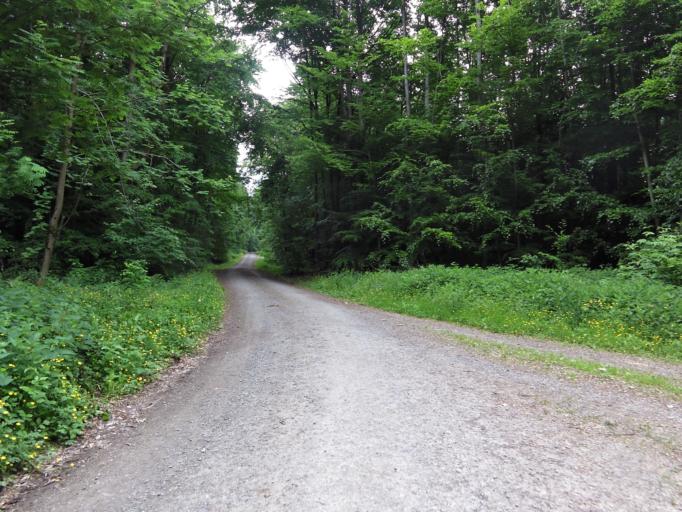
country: DE
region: Bavaria
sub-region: Regierungsbezirk Unterfranken
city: Kleinrinderfeld
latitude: 49.7117
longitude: 9.8207
